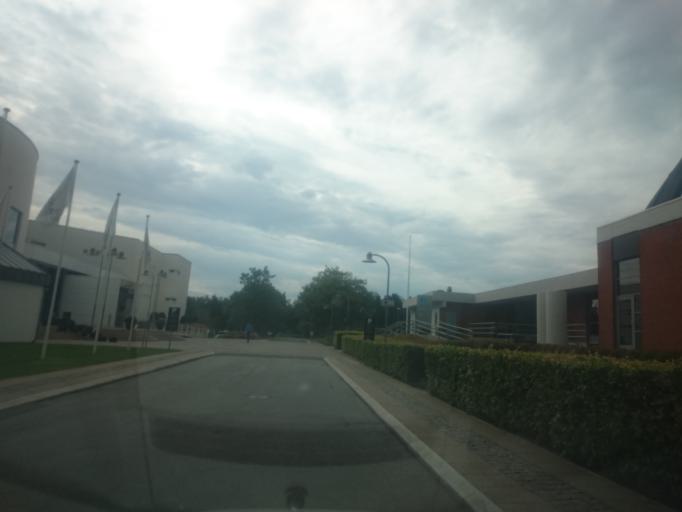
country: DK
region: South Denmark
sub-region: Billund Kommune
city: Billund
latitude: 55.7330
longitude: 9.1270
